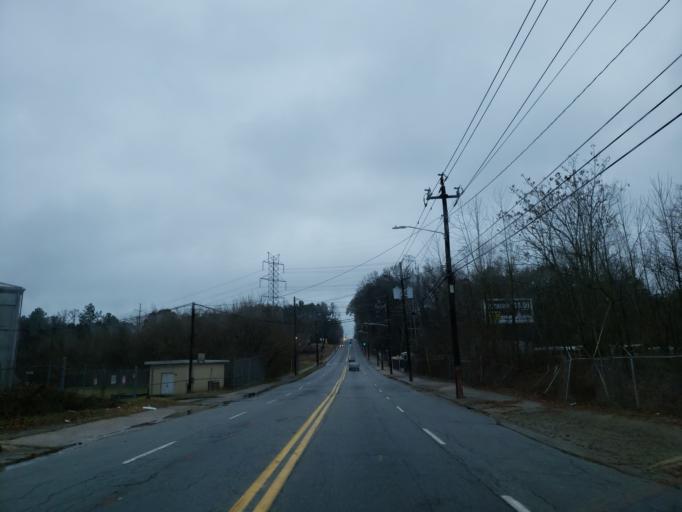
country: US
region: Georgia
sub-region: Fulton County
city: Atlanta
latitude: 33.7231
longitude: -84.3685
